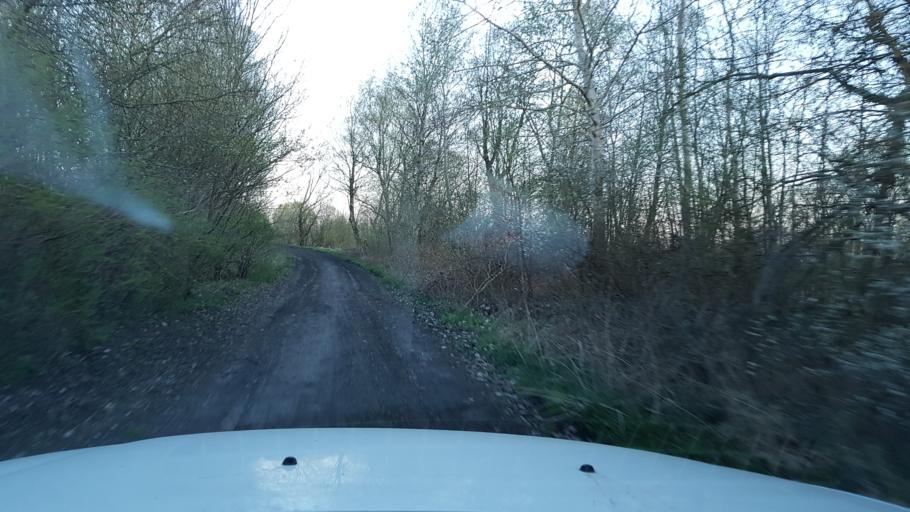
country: PL
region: West Pomeranian Voivodeship
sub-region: Powiat bialogardzki
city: Bialogard
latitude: 53.9768
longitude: 15.9563
